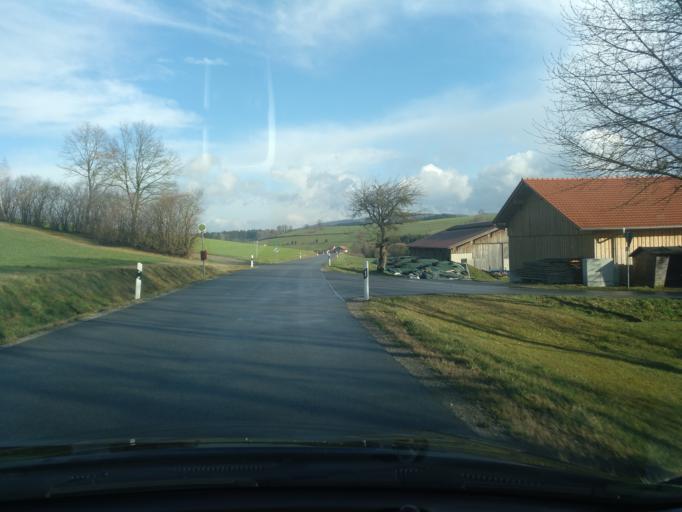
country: DE
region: Bavaria
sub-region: Upper Palatinate
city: Zandt
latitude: 49.1234
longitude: 12.7197
